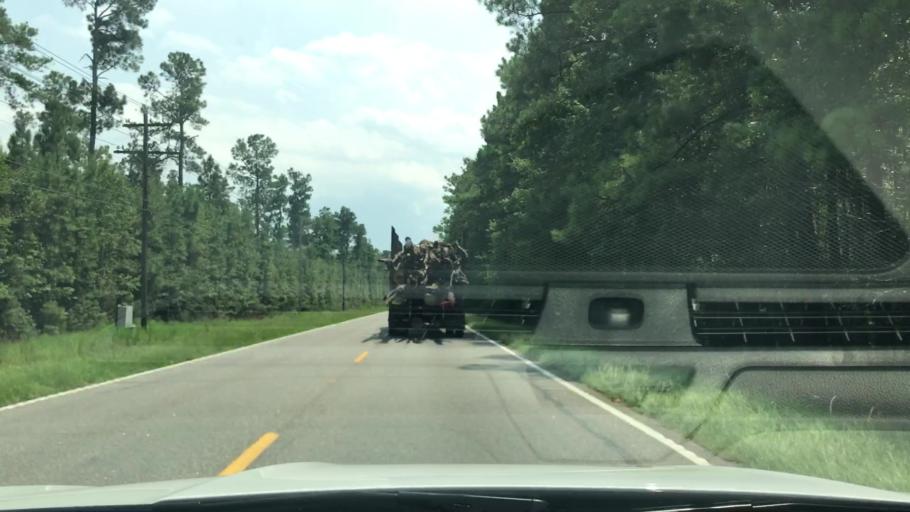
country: US
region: South Carolina
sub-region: Georgetown County
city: Georgetown
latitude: 33.4414
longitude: -79.2769
